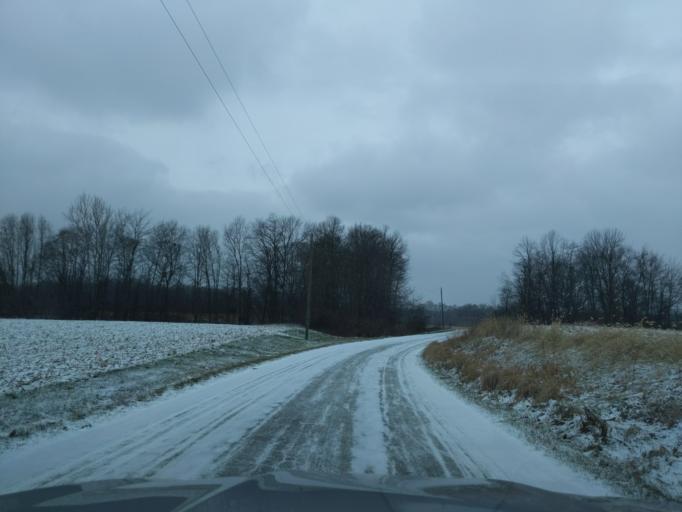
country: US
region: Indiana
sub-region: Decatur County
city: Greensburg
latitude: 39.2485
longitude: -85.4591
